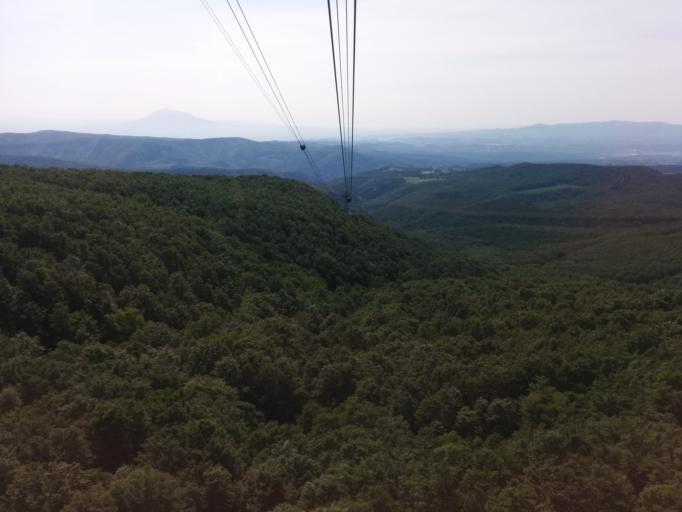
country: JP
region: Aomori
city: Aomori Shi
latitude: 40.6788
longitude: 140.8436
